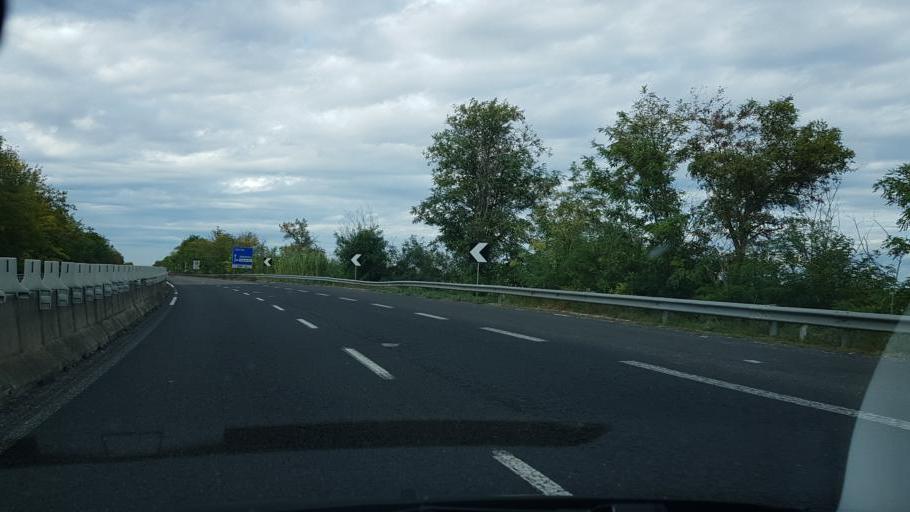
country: IT
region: Apulia
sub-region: Provincia di Lecce
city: Cavallino
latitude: 40.3138
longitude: 18.1899
